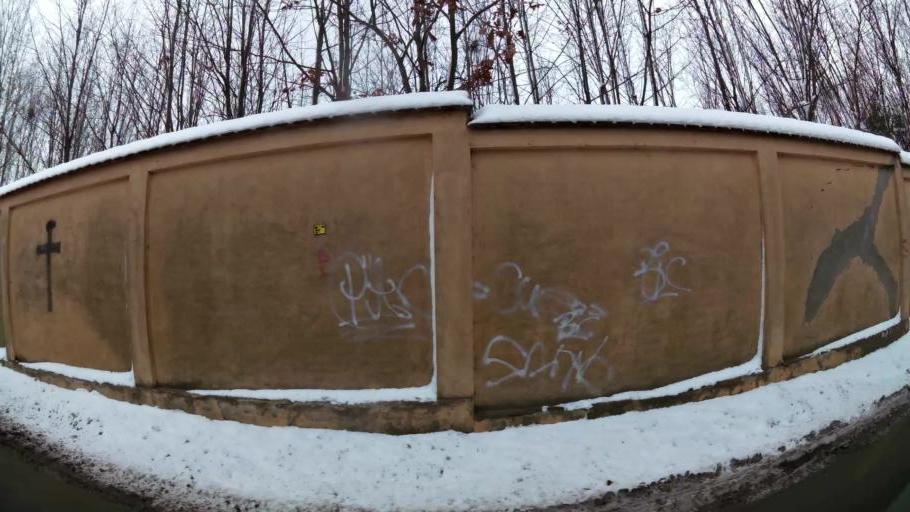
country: RO
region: Ilfov
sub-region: Comuna Tunari
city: Tunari
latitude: 44.5162
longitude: 26.1480
